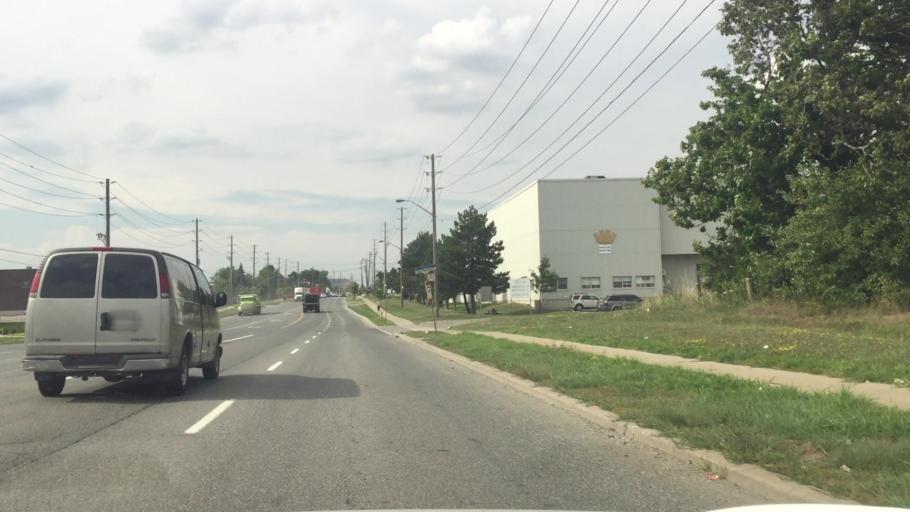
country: CA
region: Ontario
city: Concord
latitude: 43.7553
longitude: -79.5372
